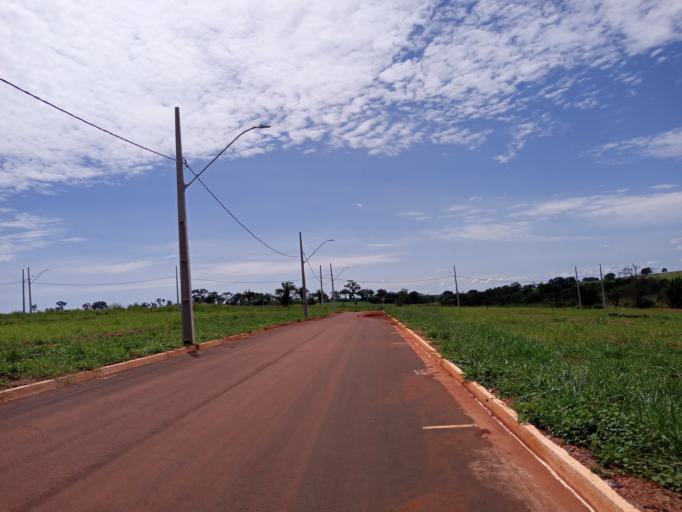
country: BR
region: Goias
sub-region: Itumbiara
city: Itumbiara
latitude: -18.4326
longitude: -49.1808
